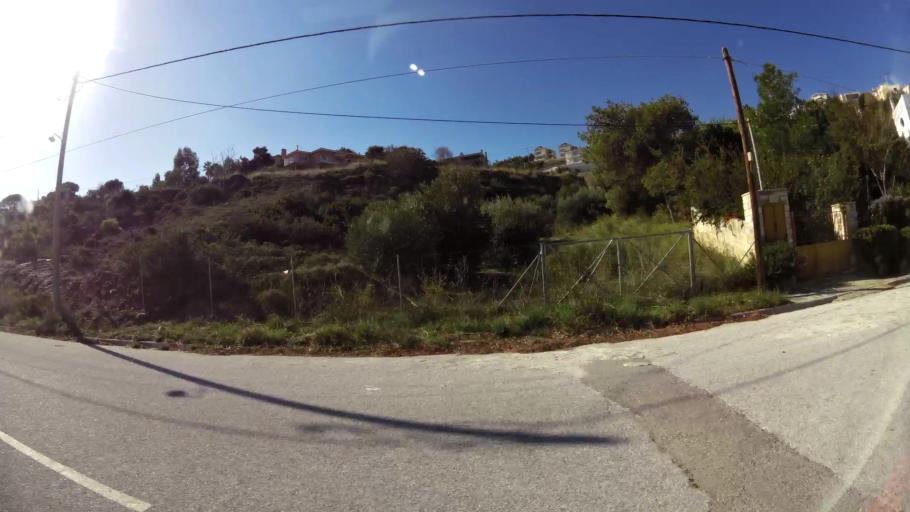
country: GR
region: Attica
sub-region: Nomarchia Anatolikis Attikis
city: Dhrafi
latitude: 38.0288
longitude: 23.9018
